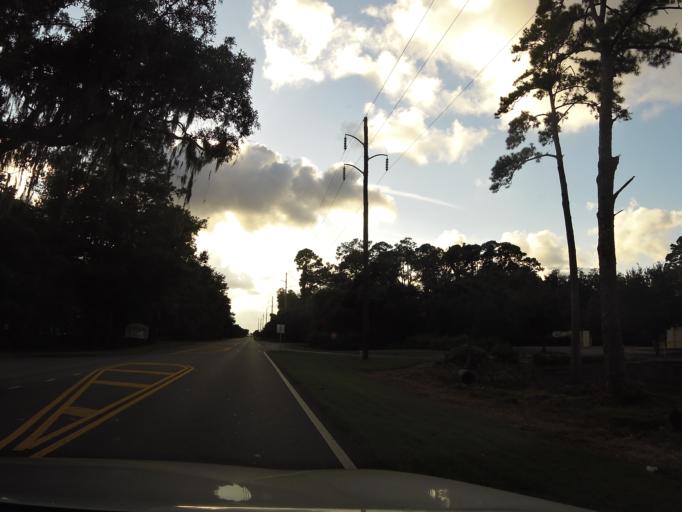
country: US
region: Georgia
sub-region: Glynn County
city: Saint Simon Mills
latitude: 31.1843
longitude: -81.3802
